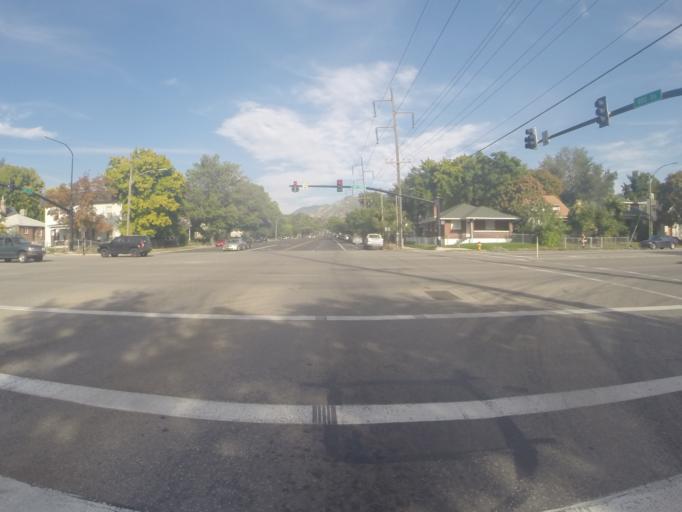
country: US
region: Utah
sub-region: Salt Lake County
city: Salt Lake City
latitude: 40.7519
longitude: -111.8714
